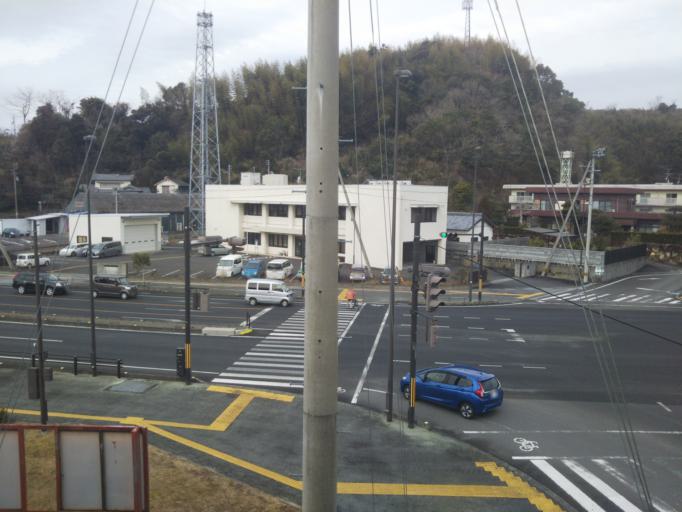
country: JP
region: Kochi
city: Nakamura
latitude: 32.9864
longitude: 132.9623
